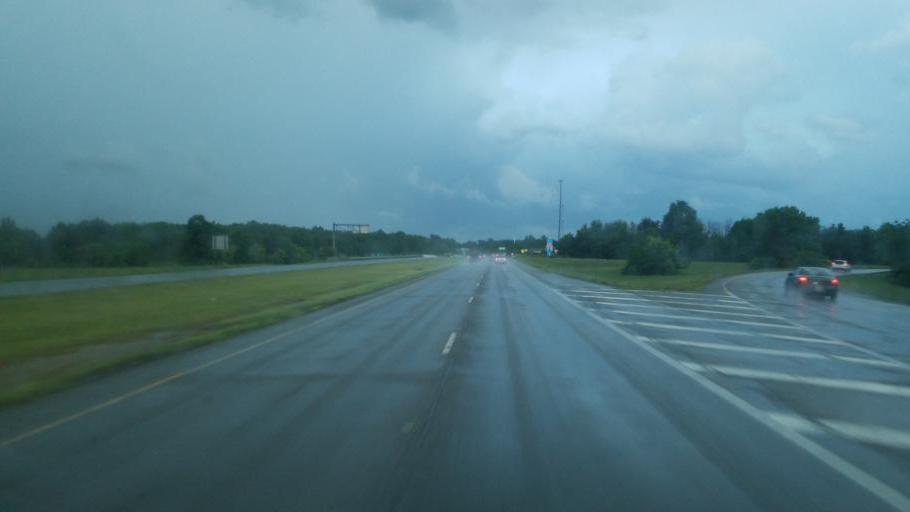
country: US
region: Ohio
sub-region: Summit County
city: Norton
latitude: 40.9963
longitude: -81.6623
